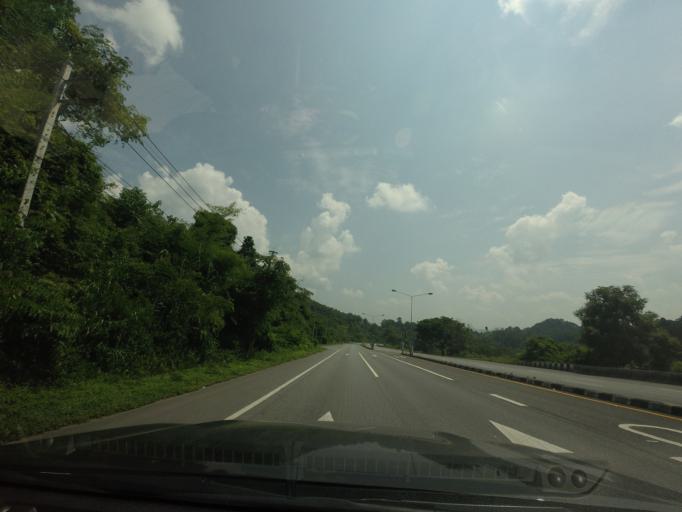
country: TH
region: Uttaradit
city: Lap Lae
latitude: 17.7768
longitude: 100.1273
